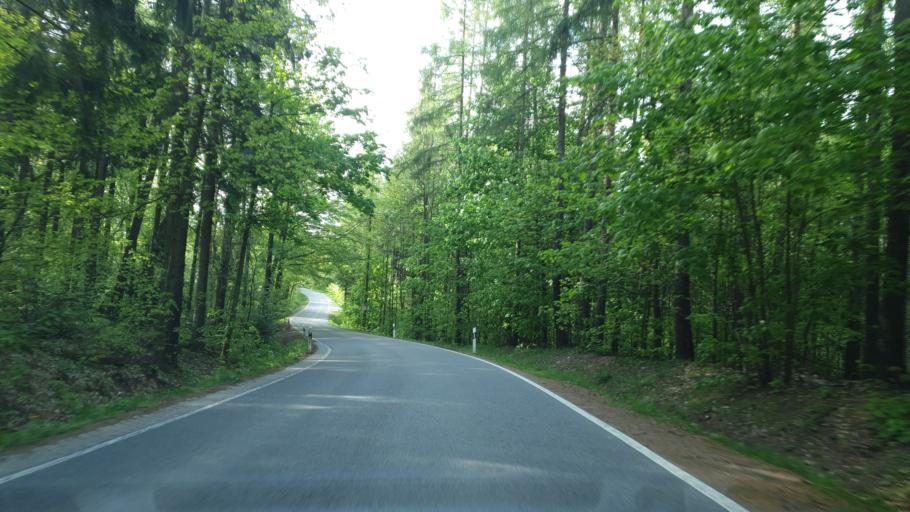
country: DE
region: Saxony
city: Oelsnitz
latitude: 50.7150
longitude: 12.6641
